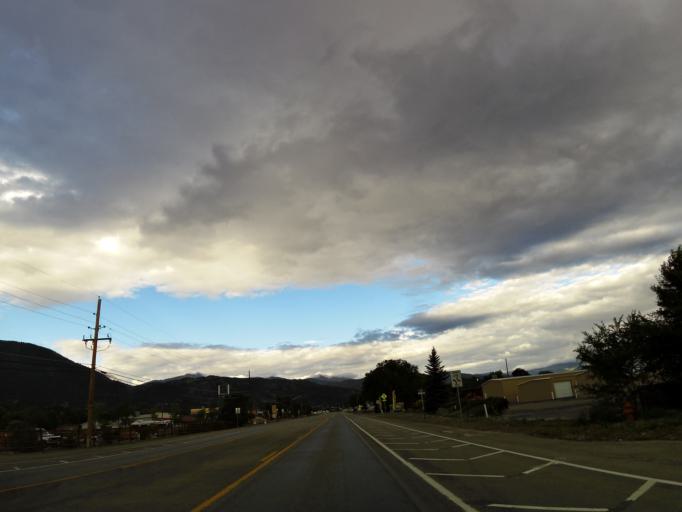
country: US
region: Colorado
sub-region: Chaffee County
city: Salida
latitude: 38.5158
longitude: -106.0692
